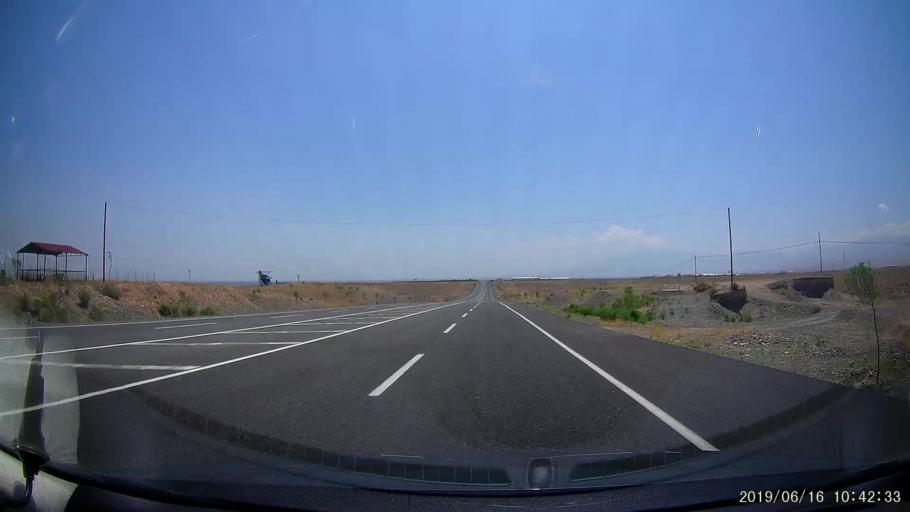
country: AM
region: Armavir
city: Shenavan
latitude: 40.0412
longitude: 43.8089
